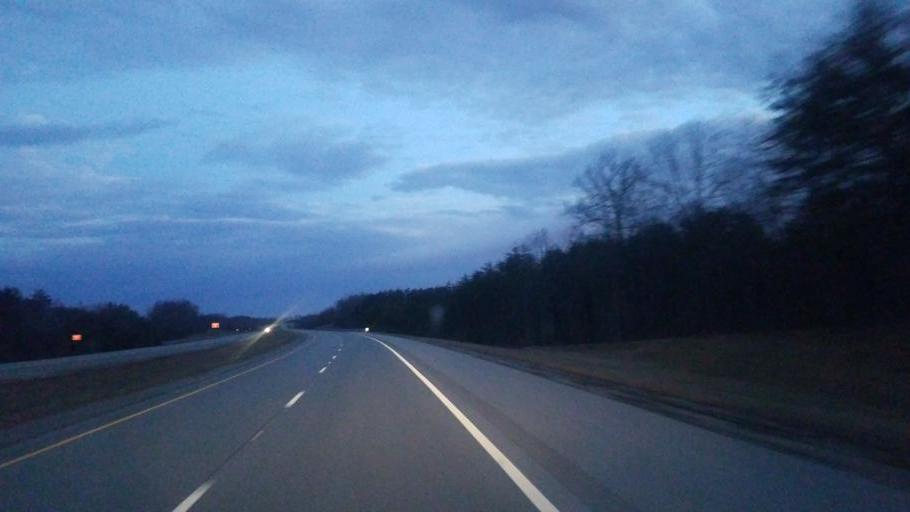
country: US
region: Tennessee
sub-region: Van Buren County
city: Spencer
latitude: 35.6055
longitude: -85.4688
